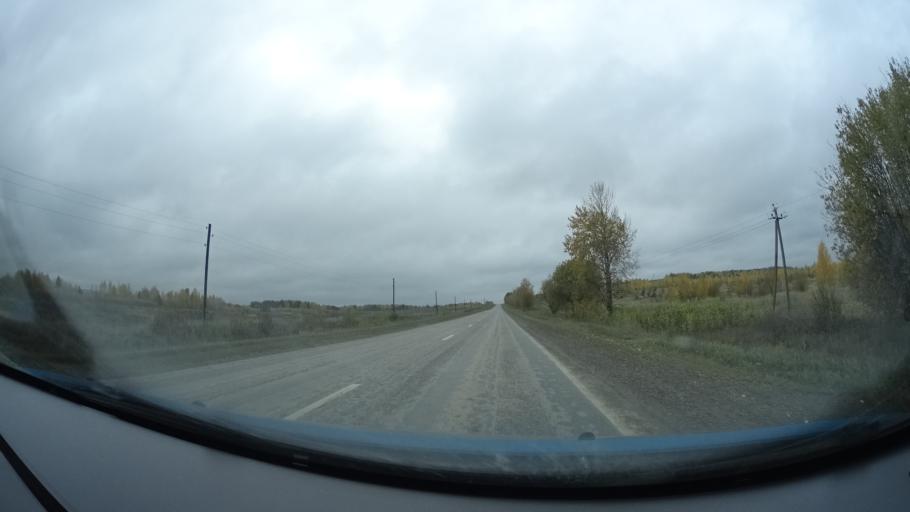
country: RU
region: Perm
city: Osa
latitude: 57.1349
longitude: 55.5267
